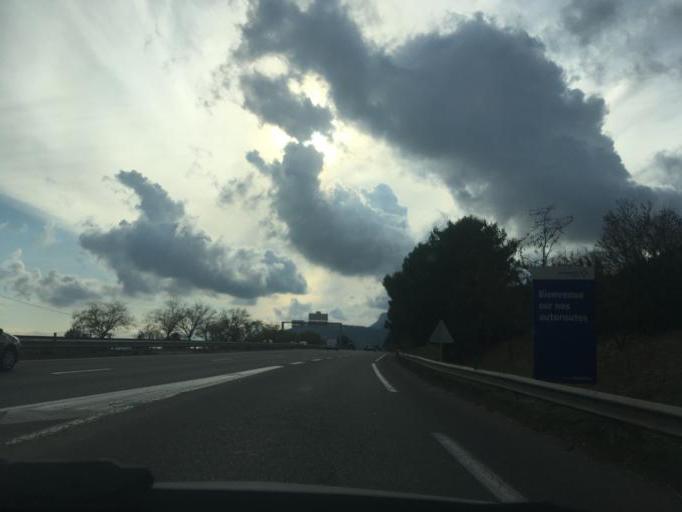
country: FR
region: Provence-Alpes-Cote d'Azur
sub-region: Departement du Var
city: Cuers
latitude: 43.2226
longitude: 6.0697
